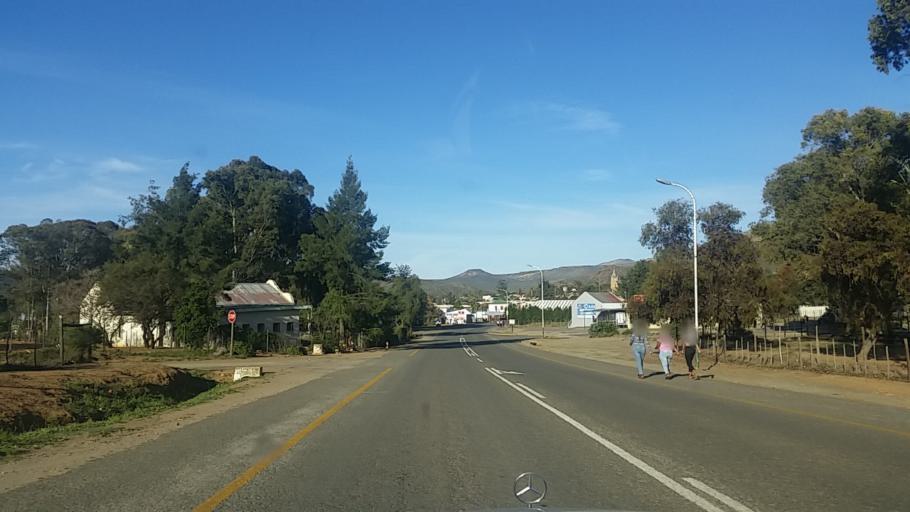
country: ZA
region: Western Cape
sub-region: Eden District Municipality
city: Knysna
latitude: -33.6594
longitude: 23.1164
